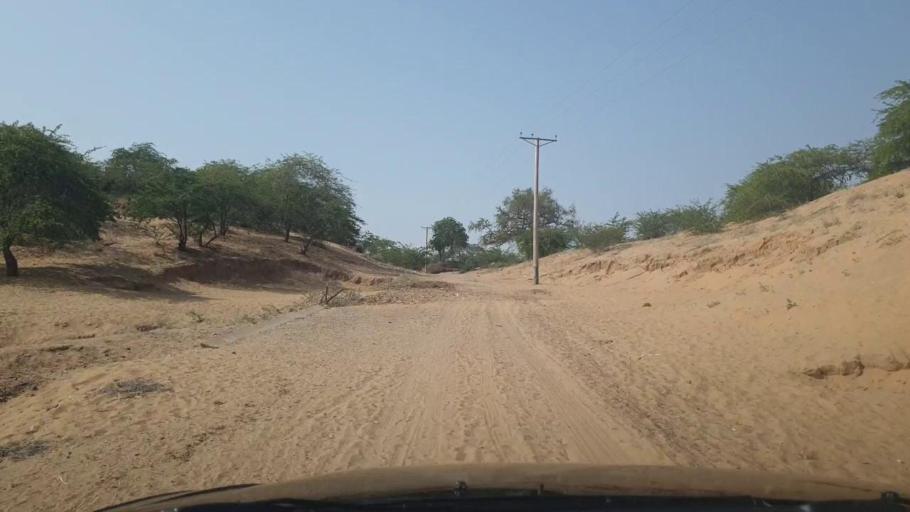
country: PK
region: Sindh
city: Islamkot
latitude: 24.9992
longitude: 70.2056
